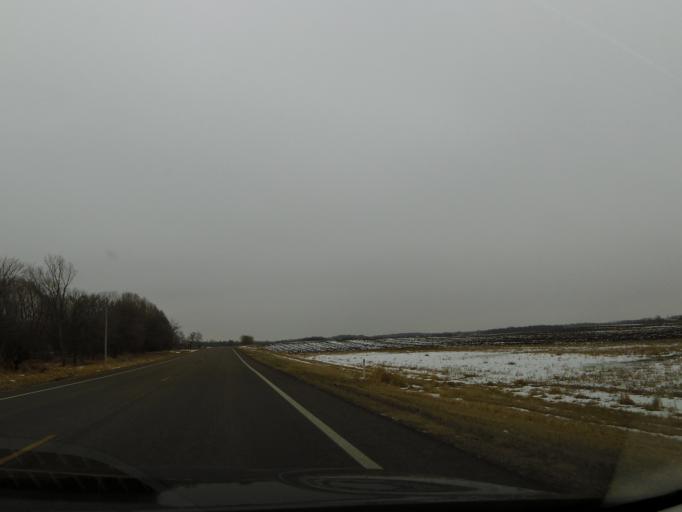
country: US
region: Minnesota
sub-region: Scott County
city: Prior Lake
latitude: 44.6305
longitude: -93.4957
